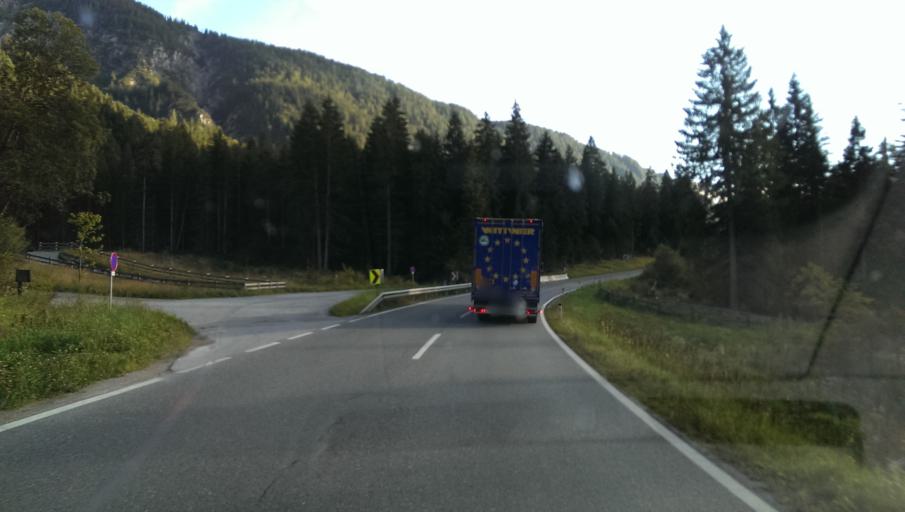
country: AT
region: Tyrol
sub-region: Politischer Bezirk Innsbruck Land
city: Seefeld in Tirol
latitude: 47.3582
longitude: 11.2266
